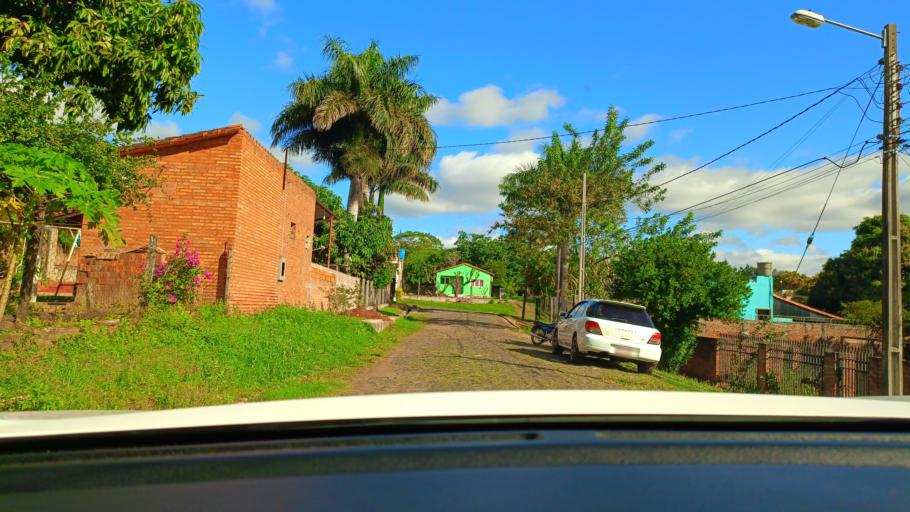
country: PY
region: San Pedro
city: Guayaybi
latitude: -24.6696
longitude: -56.4473
